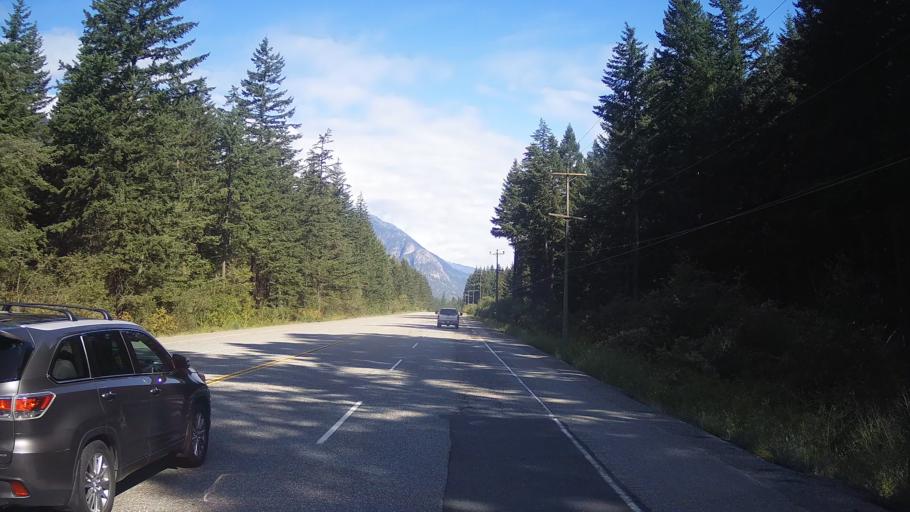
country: CA
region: British Columbia
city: Hope
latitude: 50.0413
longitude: -121.5361
